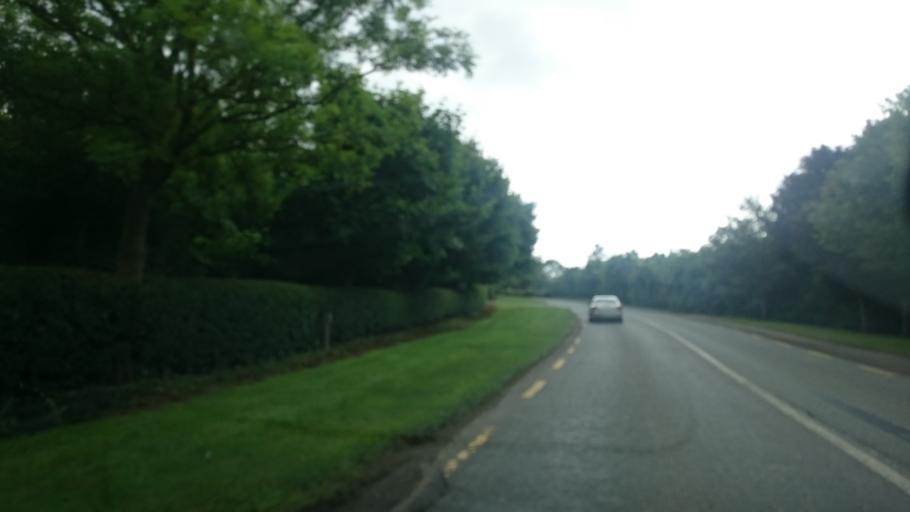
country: IE
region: Leinster
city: Lusk
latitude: 53.5168
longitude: -6.1716
